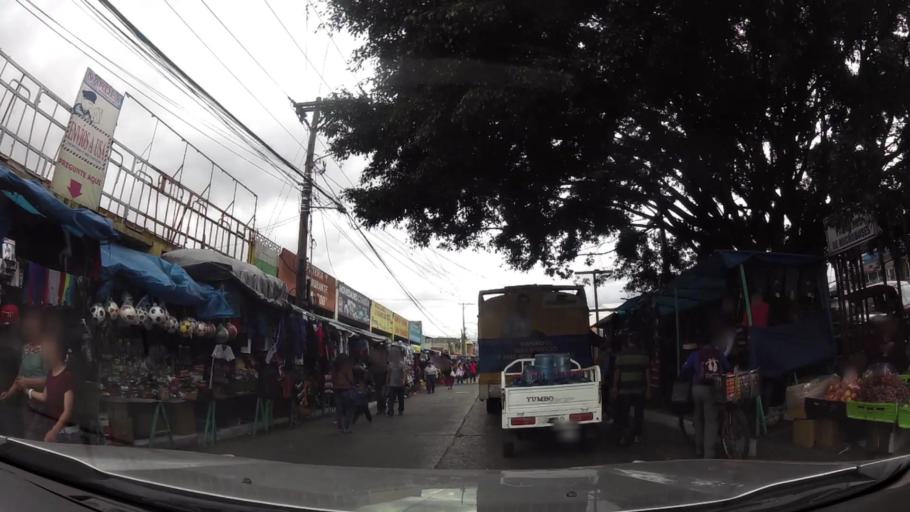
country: GT
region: Guatemala
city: Mixco
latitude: 14.6510
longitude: -90.5853
